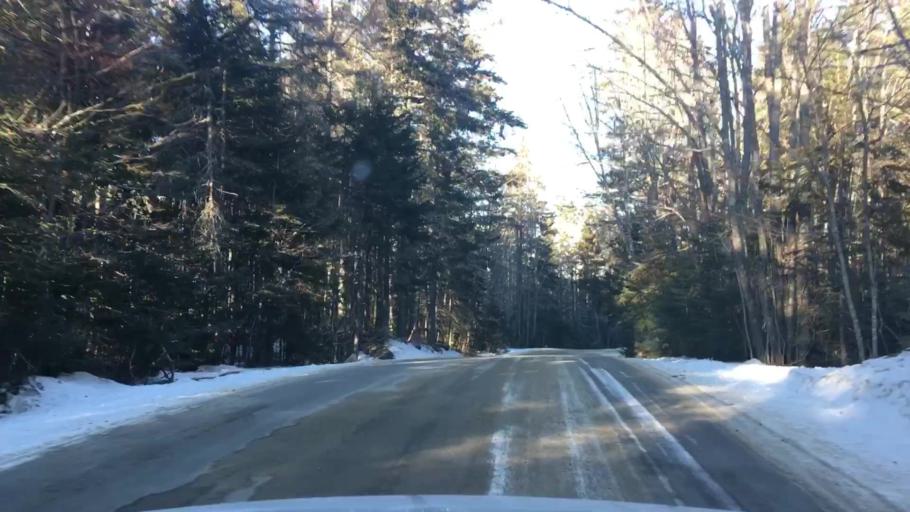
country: US
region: Maine
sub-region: Hancock County
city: Castine
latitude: 44.3839
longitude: -68.7452
